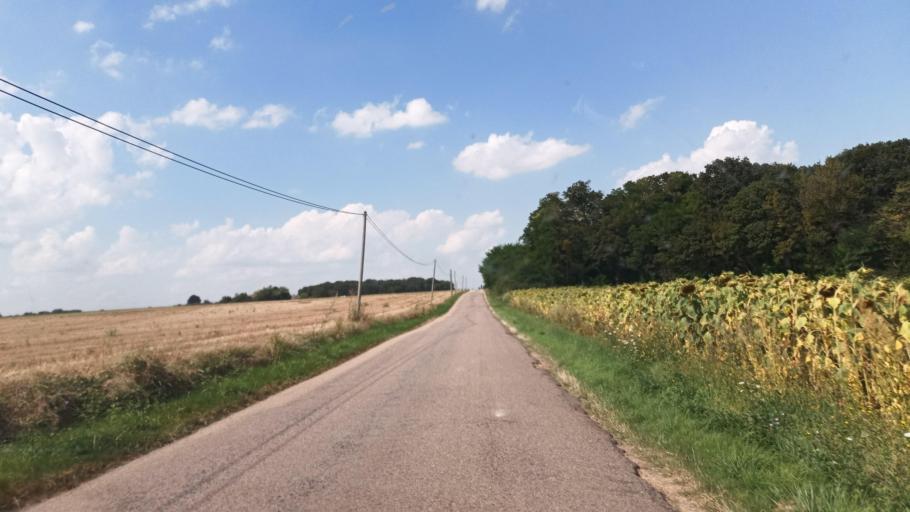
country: FR
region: Bourgogne
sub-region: Departement de l'Yonne
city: Egriselles-le-Bocage
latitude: 48.0335
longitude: 3.1640
